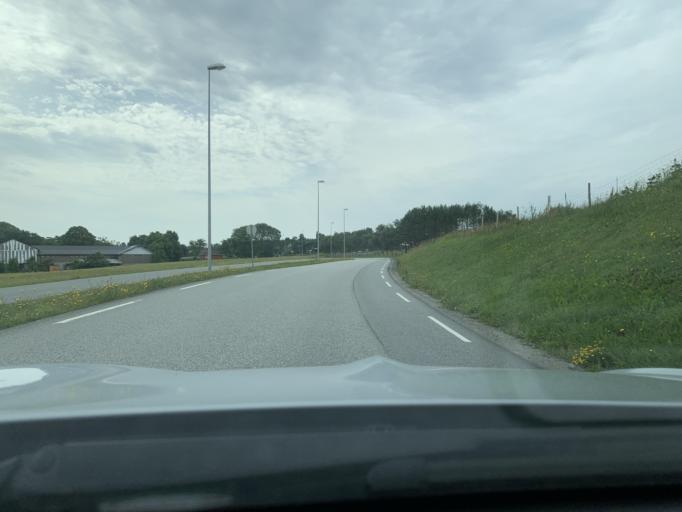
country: NO
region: Rogaland
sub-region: Time
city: Bryne
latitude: 58.7621
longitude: 5.7108
